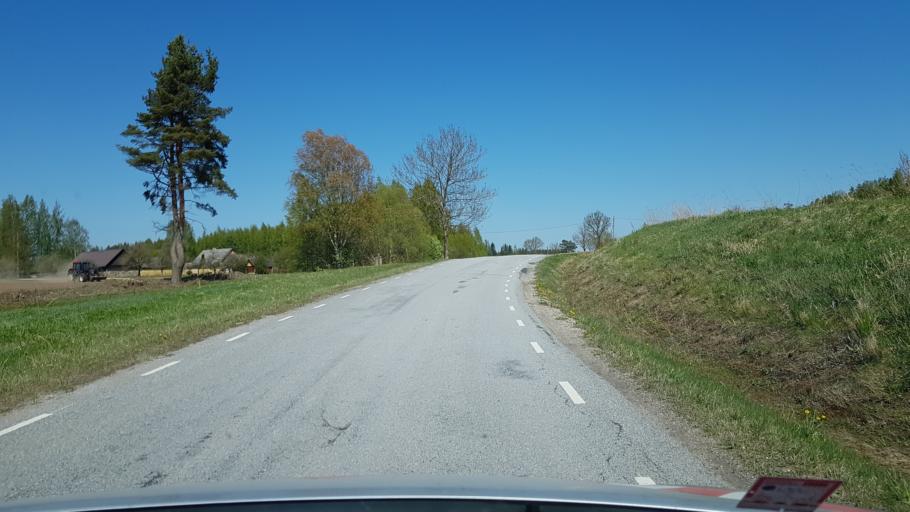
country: EE
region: Vorumaa
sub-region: Voru linn
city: Voru
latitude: 57.9261
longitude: 26.9512
